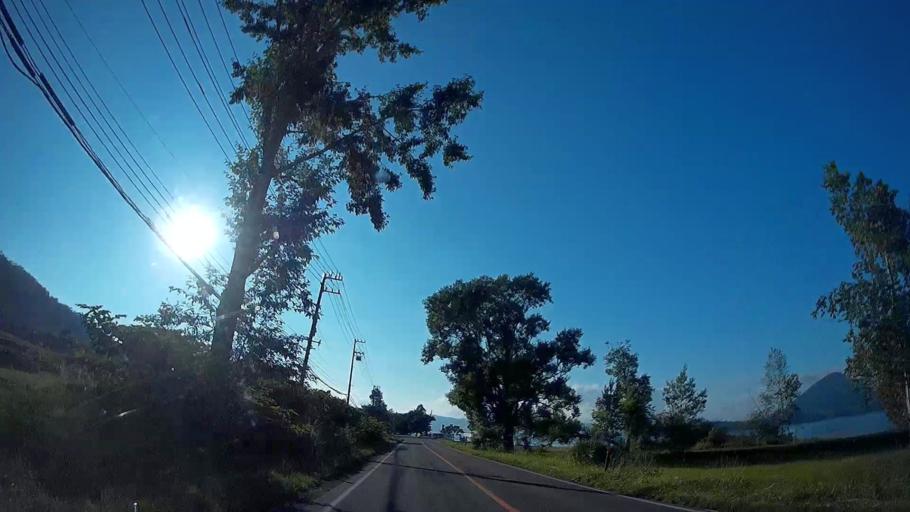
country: JP
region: Hokkaido
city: Date
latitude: 42.5628
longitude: 140.8459
